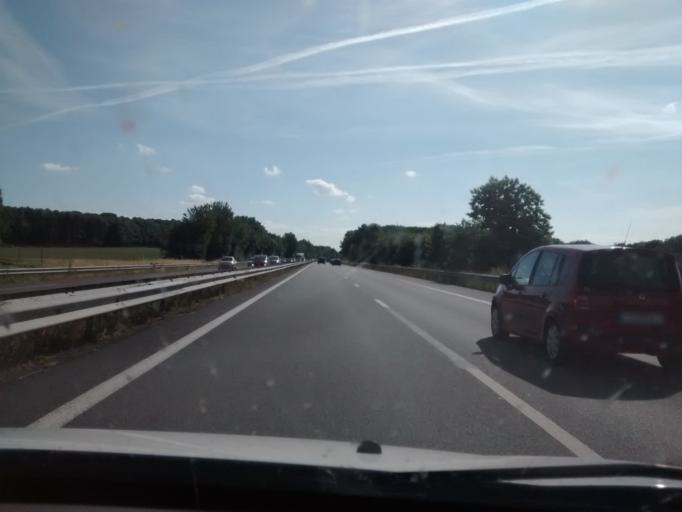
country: FR
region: Brittany
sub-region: Departement d'Ille-et-Vilaine
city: Argentre-du-Plessis
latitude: 48.0765
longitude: -1.1475
